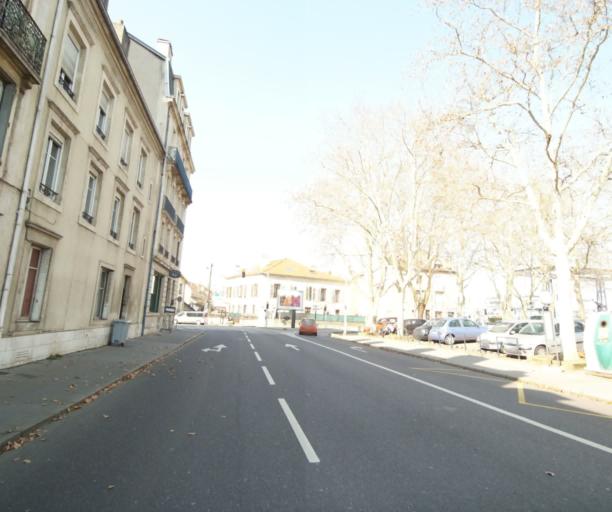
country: FR
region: Lorraine
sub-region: Departement de Meurthe-et-Moselle
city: Malzeville
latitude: 48.7024
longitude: 6.1817
